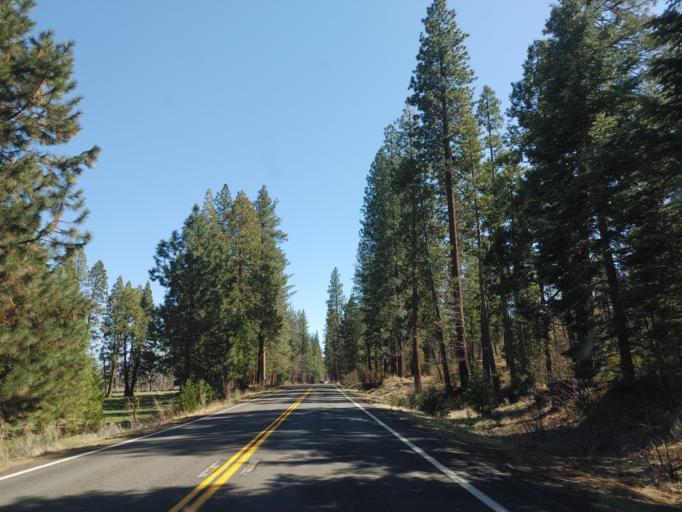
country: US
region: California
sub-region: Shasta County
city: Burney
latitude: 40.7961
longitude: -121.5095
